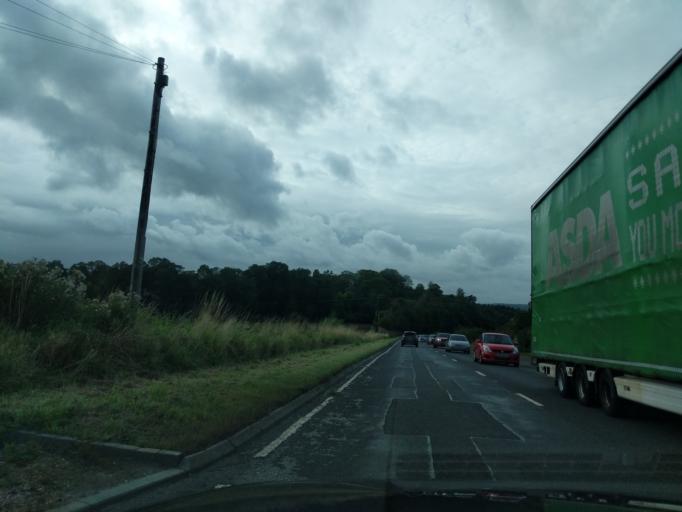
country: GB
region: Scotland
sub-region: Midlothian
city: Gorebridge
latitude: 55.8378
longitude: -3.0544
